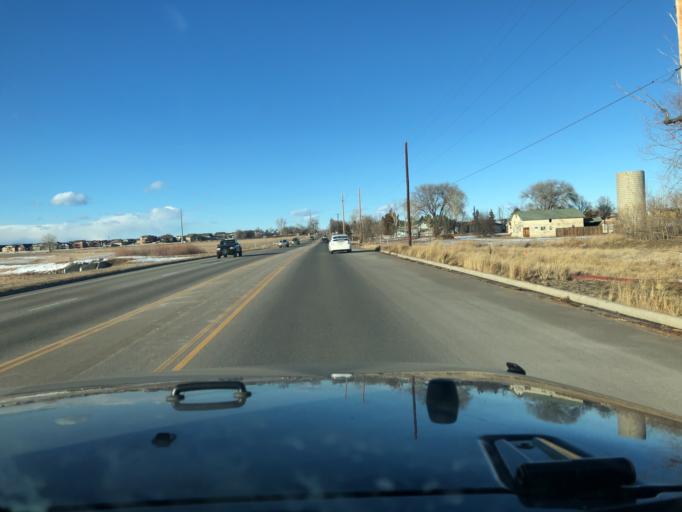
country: US
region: Colorado
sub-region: Boulder County
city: Longmont
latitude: 40.1762
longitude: -105.0552
